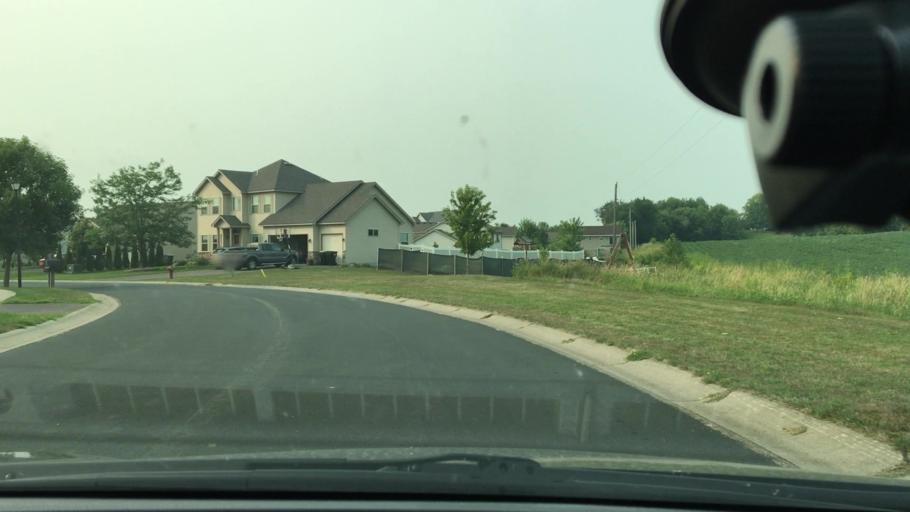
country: US
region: Minnesota
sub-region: Wright County
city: Albertville
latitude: 45.2537
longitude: -93.6531
